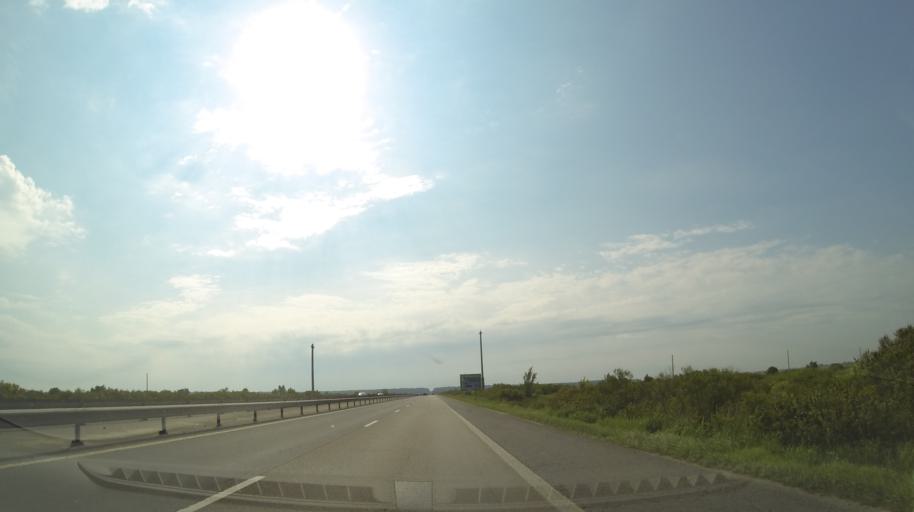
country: RO
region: Giurgiu
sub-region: Comuna Vanatorii Mici
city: Vanatorii Mari
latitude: 44.5237
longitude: 25.5462
